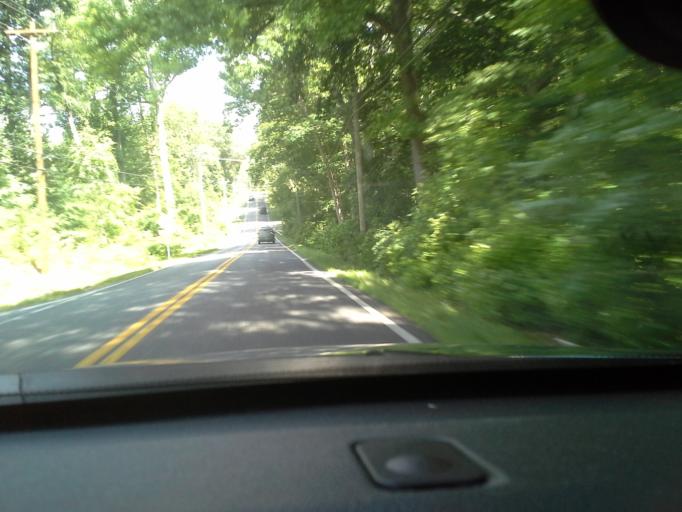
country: US
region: Maryland
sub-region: Calvert County
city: Owings
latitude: 38.7012
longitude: -76.6184
